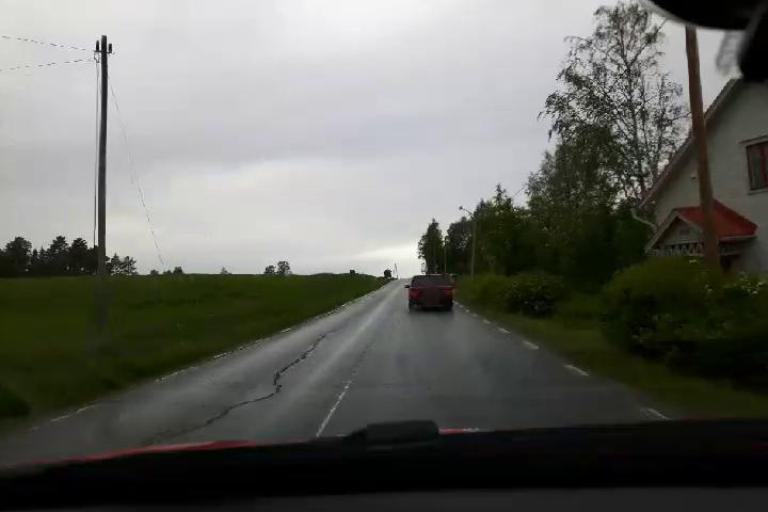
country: SE
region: Jaemtland
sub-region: Bergs Kommun
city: Hoverberg
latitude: 62.8119
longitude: 14.4258
